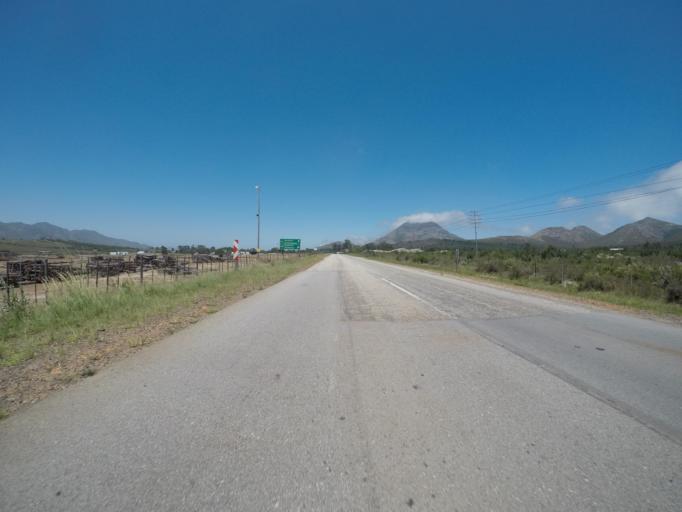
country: ZA
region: Eastern Cape
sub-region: Cacadu District Municipality
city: Kareedouw
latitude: -33.9483
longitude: 24.2789
